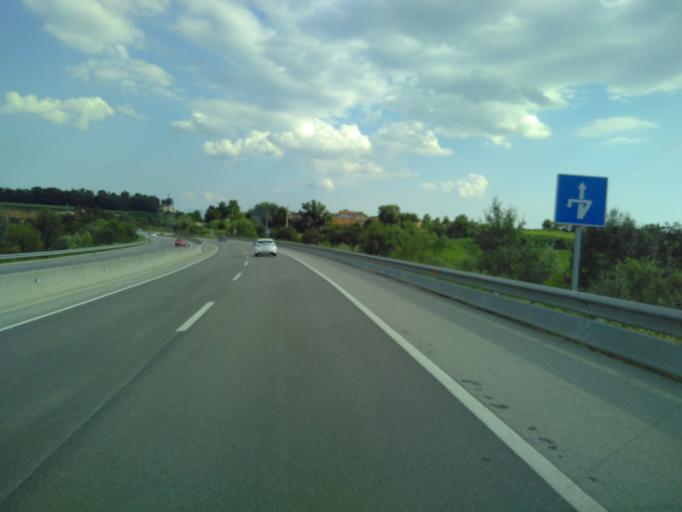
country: ES
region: Catalonia
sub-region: Provincia de Barcelona
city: Santa Cecilia de Voltrega
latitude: 42.0278
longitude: 2.2399
